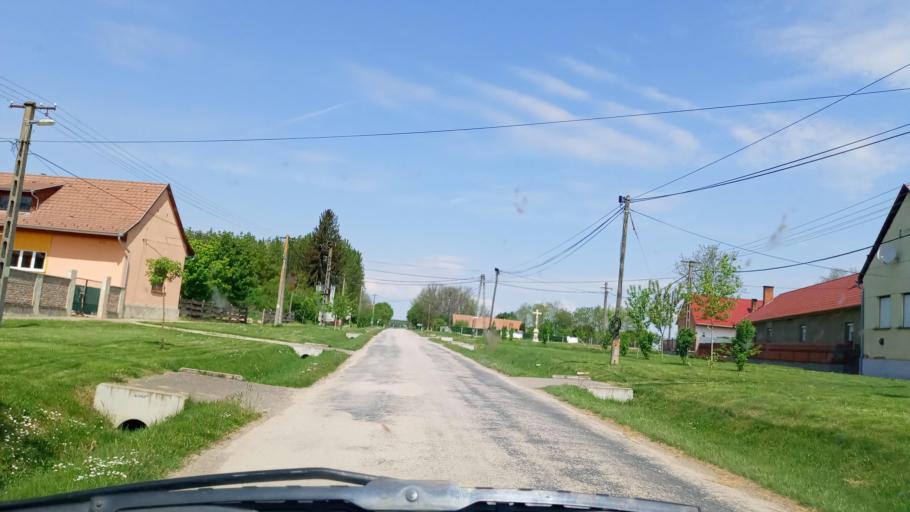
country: HR
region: Osjecko-Baranjska
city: Beli Manastir
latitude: 45.8698
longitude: 18.5842
